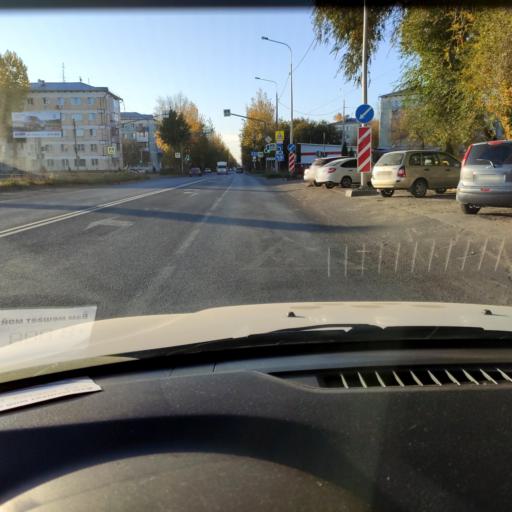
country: RU
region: Samara
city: Tol'yatti
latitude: 53.5384
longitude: 49.4095
